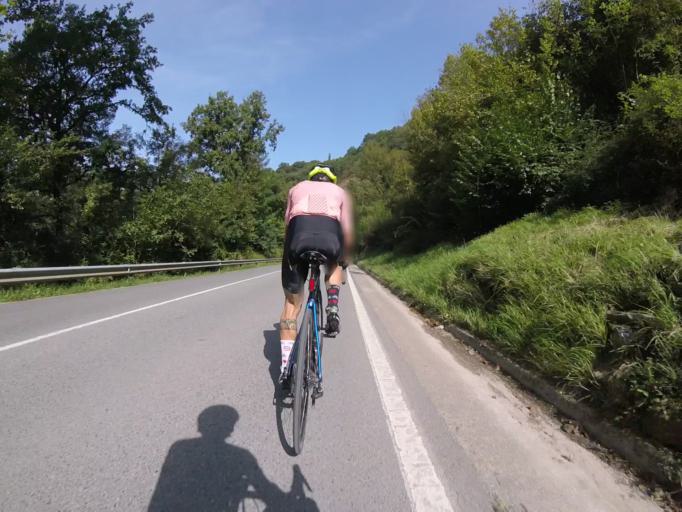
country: ES
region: Navarre
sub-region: Provincia de Navarra
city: Doneztebe
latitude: 43.1433
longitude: -1.5964
